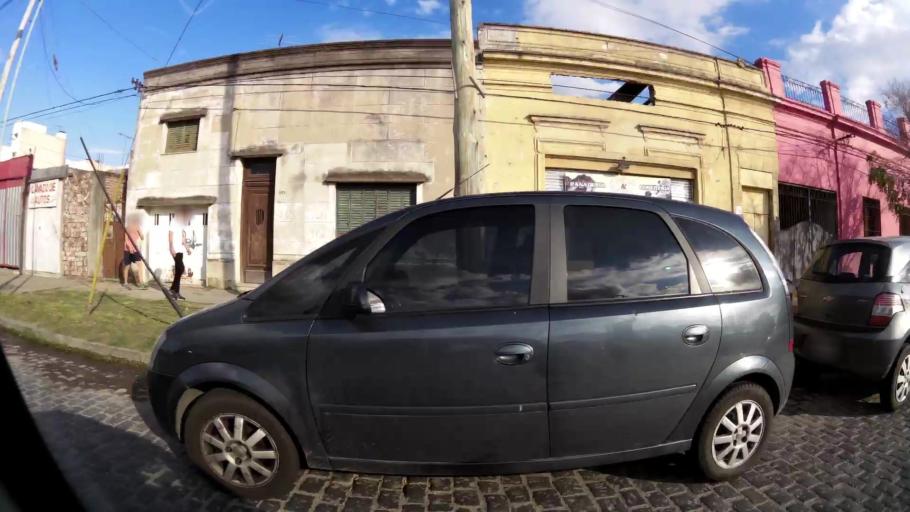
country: AR
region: Buenos Aires
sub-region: Partido de La Plata
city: La Plata
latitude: -34.8915
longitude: -57.9666
